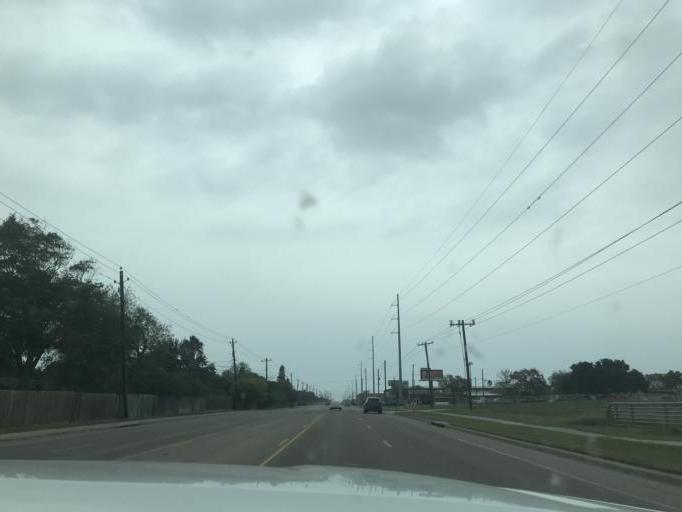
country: US
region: Texas
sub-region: Nueces County
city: Corpus Christi
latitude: 27.6965
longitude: -97.3725
